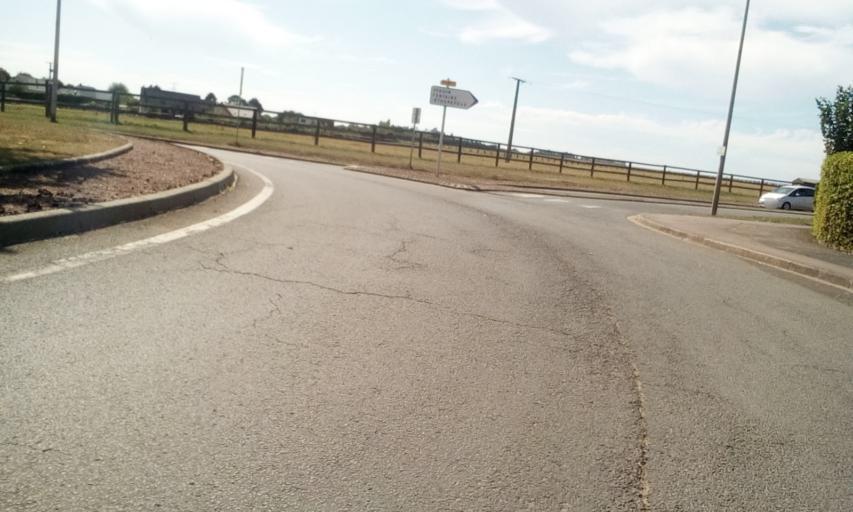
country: FR
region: Lower Normandy
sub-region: Departement du Calvados
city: Eterville
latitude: 49.1279
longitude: -0.4237
